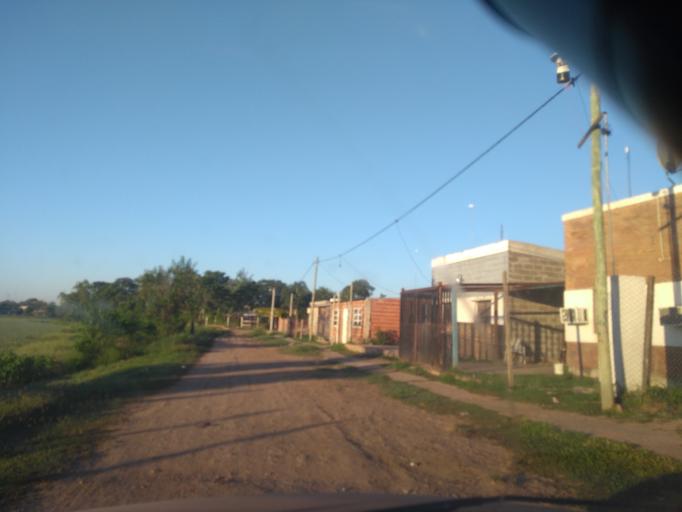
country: AR
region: Chaco
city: Resistencia
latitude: -27.4583
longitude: -58.9682
